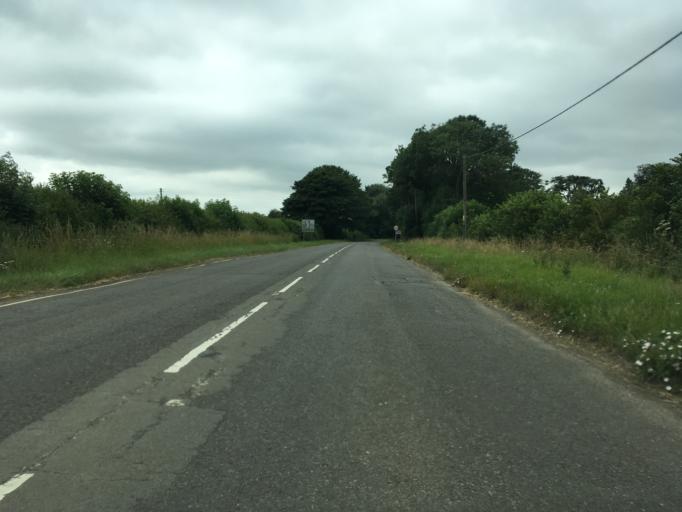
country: GB
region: England
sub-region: Buckinghamshire
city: Buckingham
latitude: 51.9893
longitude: -1.0656
